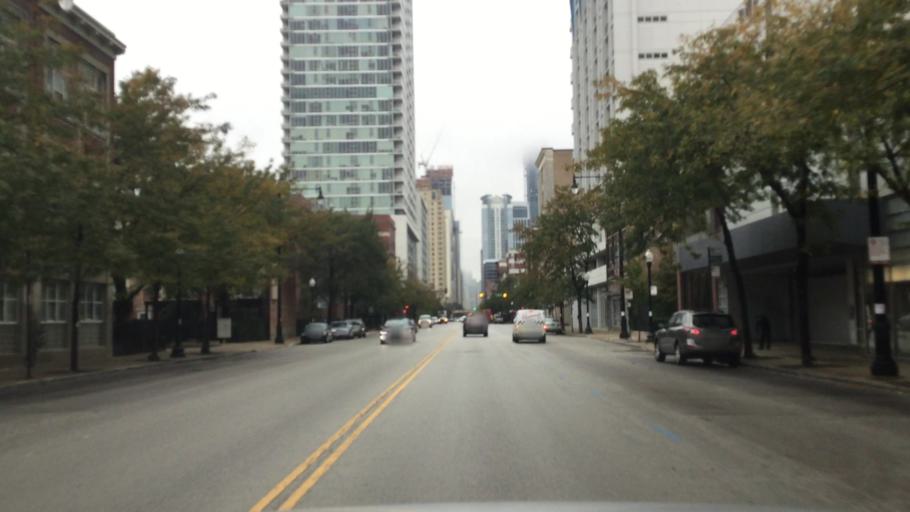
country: US
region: Illinois
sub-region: Cook County
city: Chicago
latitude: 41.8564
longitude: -87.6241
